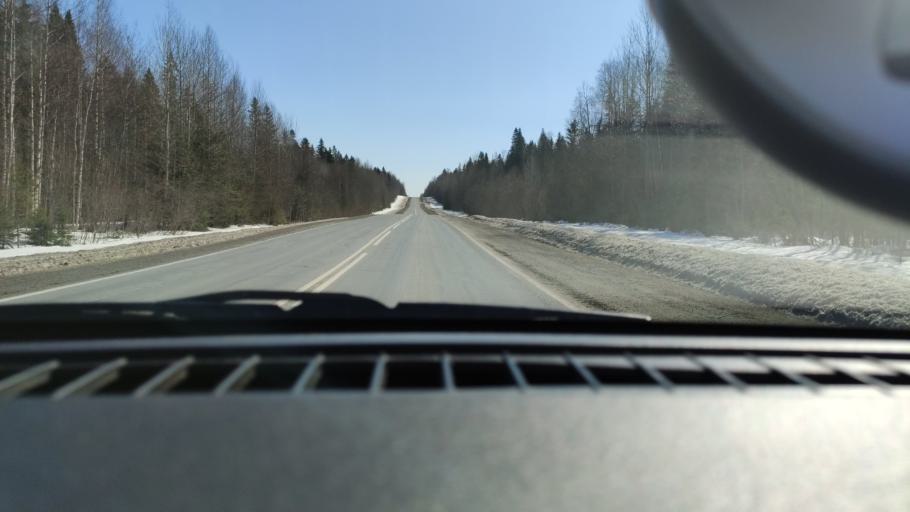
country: RU
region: Perm
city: Perm
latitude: 58.1593
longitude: 56.2472
